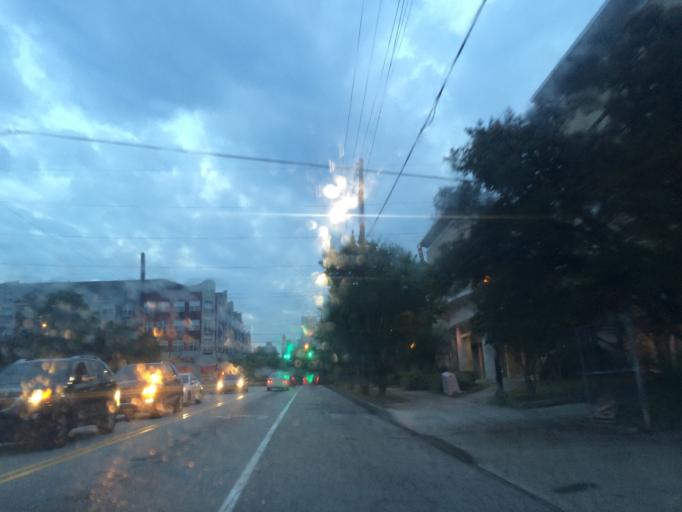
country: US
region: Georgia
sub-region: Fulton County
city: Atlanta
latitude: 33.7613
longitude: -84.3710
